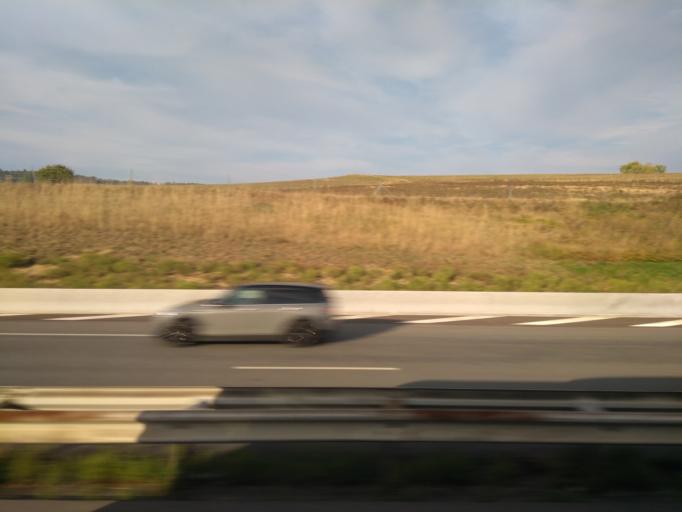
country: FR
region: Rhone-Alpes
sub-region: Departement de l'Isere
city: Cessieu
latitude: 45.5516
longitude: 5.3635
